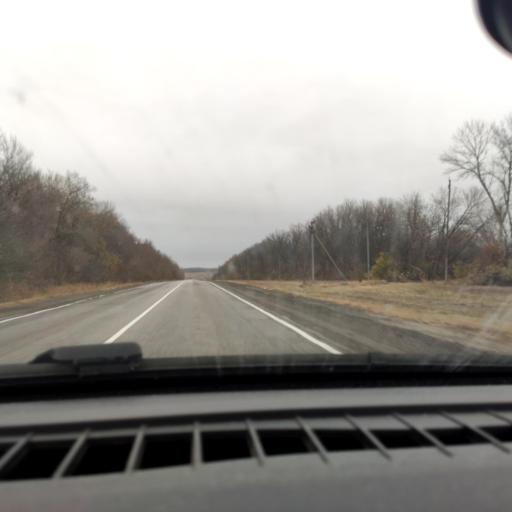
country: RU
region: Voronezj
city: Uryv-Pokrovka
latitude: 51.1091
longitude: 39.0239
